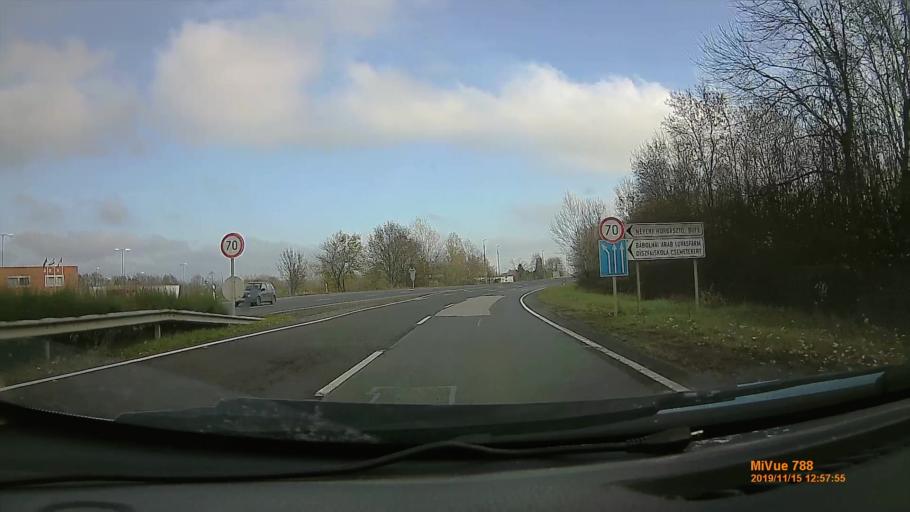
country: HU
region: Bekes
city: Bekescsaba
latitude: 46.6729
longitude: 21.1718
